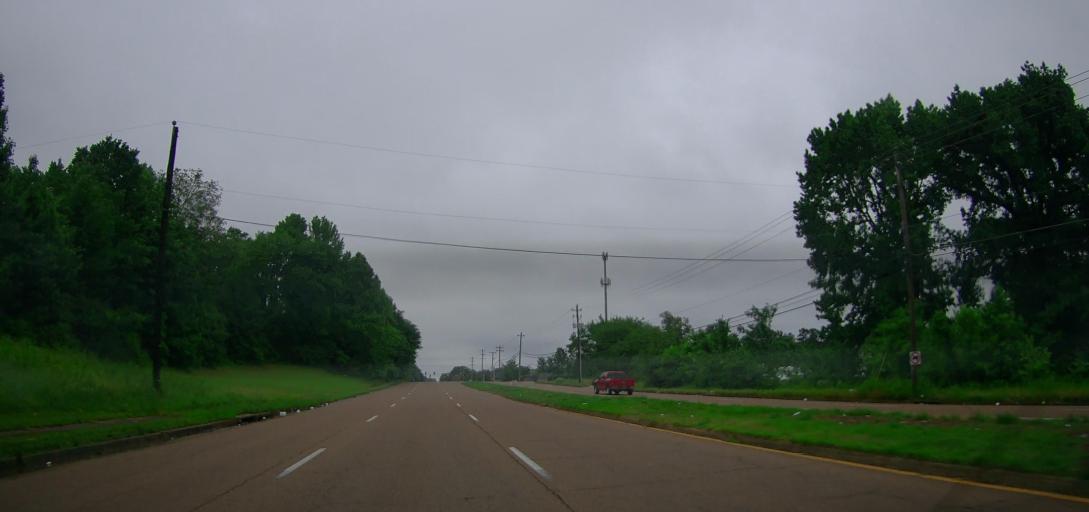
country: US
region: Mississippi
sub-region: De Soto County
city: Olive Branch
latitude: 35.0032
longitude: -89.8310
